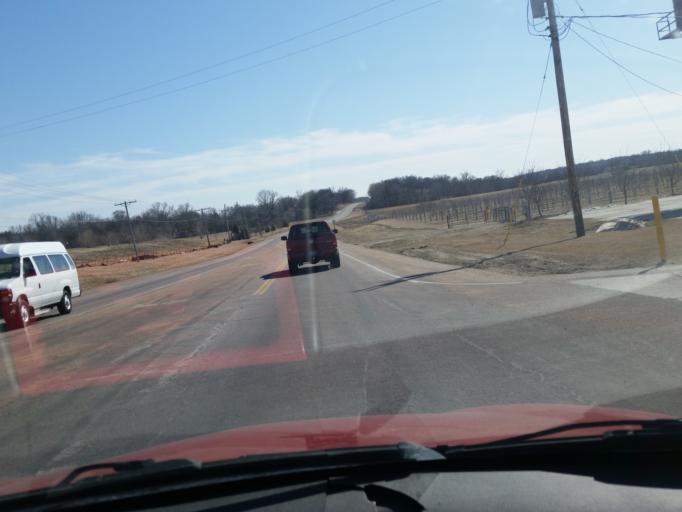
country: US
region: Nebraska
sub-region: Sarpy County
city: Offutt Air Force Base
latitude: 41.1600
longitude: -95.9670
